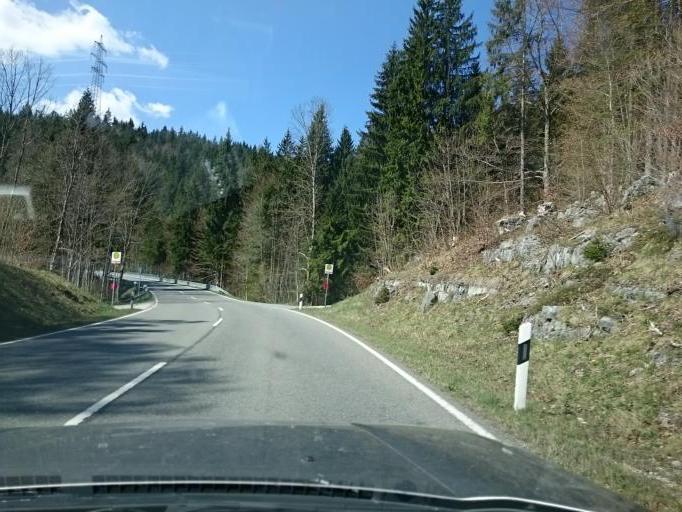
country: DE
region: Bavaria
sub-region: Upper Bavaria
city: Schlehdorf
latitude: 47.5826
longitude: 11.3060
